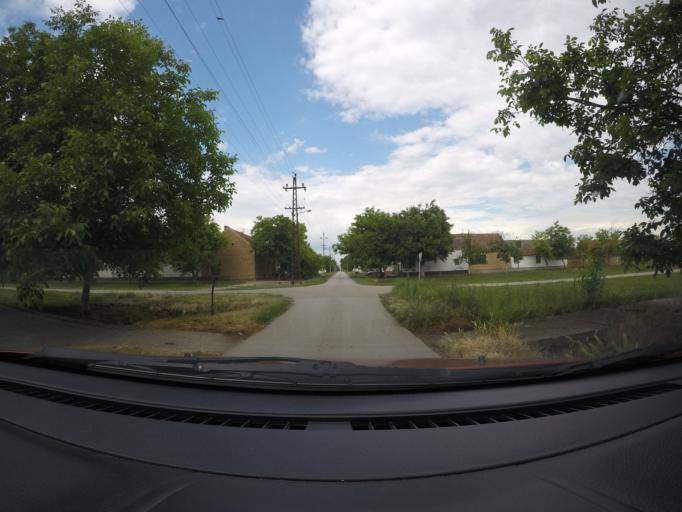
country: RS
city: Begejci
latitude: 45.5026
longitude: 20.6028
